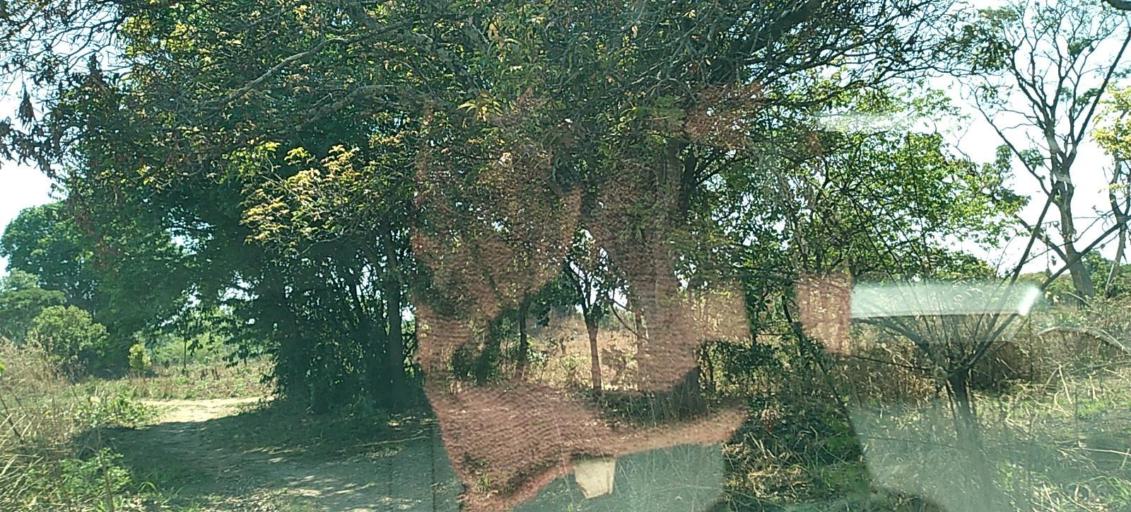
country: ZM
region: Copperbelt
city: Chililabombwe
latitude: -12.2905
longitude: 27.8940
